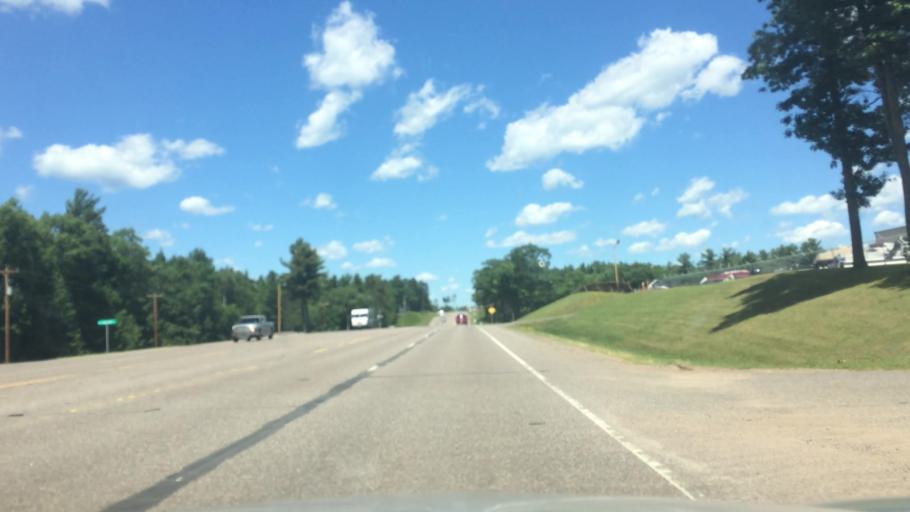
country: US
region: Wisconsin
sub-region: Vilas County
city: Lac du Flambeau
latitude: 45.8434
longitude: -89.7062
